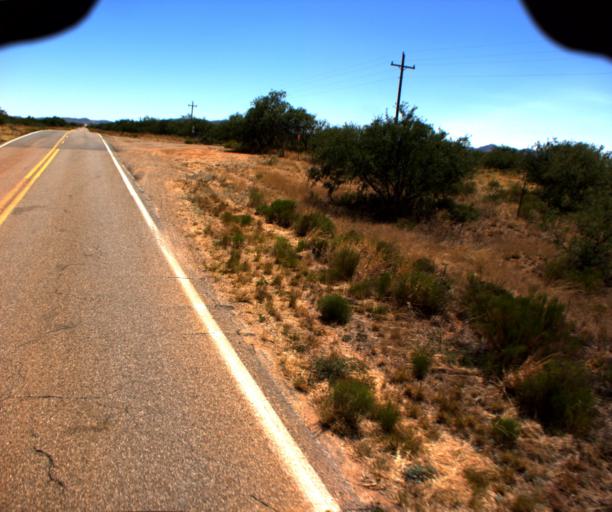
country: US
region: Arizona
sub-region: Pima County
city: Sells
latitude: 31.6125
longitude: -111.5182
